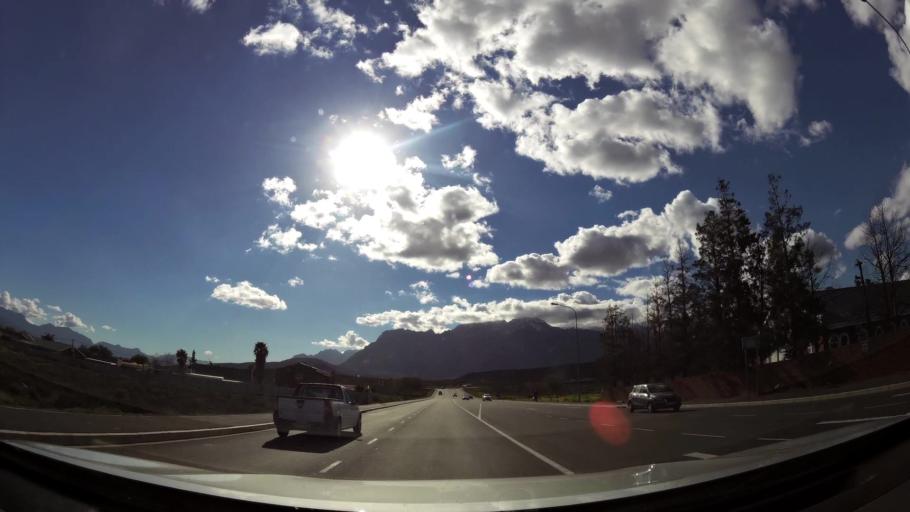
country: ZA
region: Western Cape
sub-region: Cape Winelands District Municipality
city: Worcester
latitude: -33.6376
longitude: 19.4297
